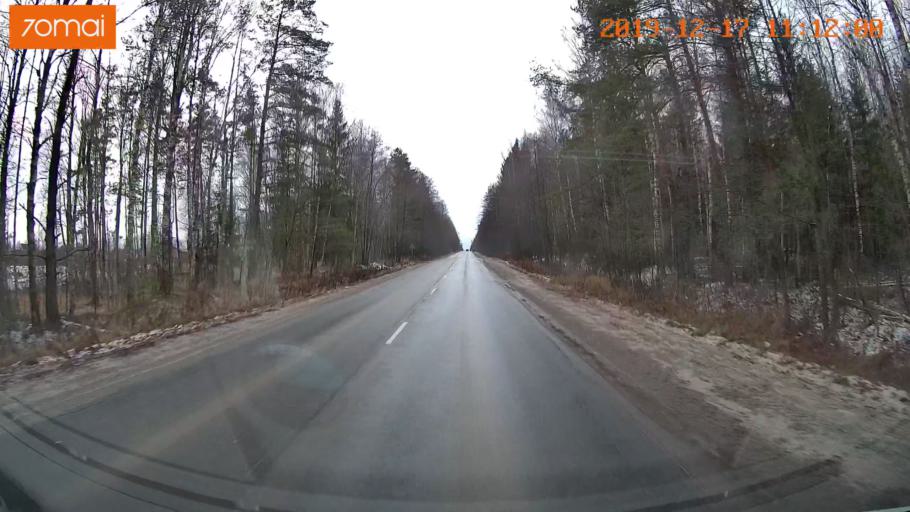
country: RU
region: Vladimir
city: Gus'-Khrustal'nyy
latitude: 55.5812
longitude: 40.6326
